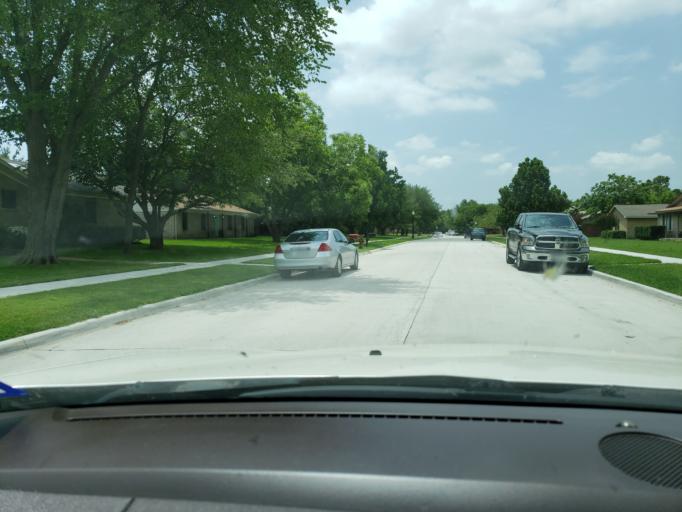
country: US
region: Texas
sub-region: Dallas County
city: Rowlett
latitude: 32.8992
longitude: -96.5641
